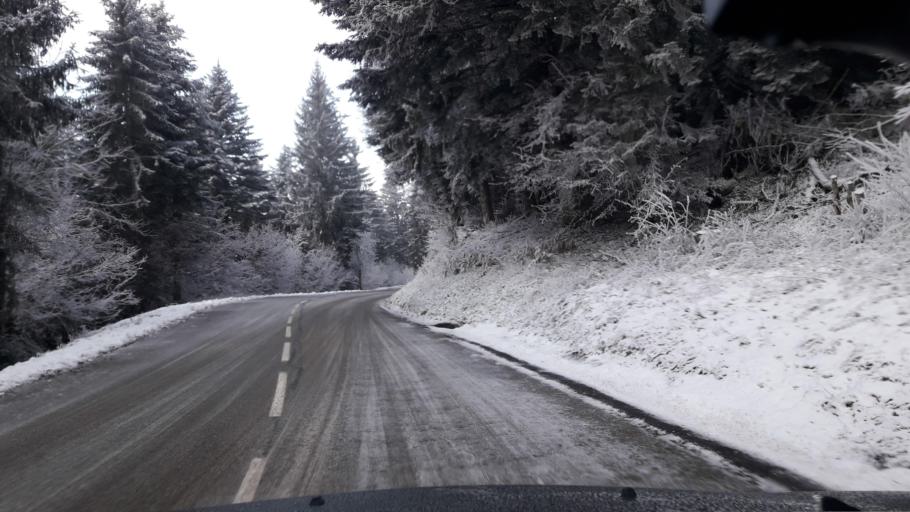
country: FR
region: Rhone-Alpes
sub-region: Departement de l'Isere
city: Allevard
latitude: 45.3973
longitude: 6.1047
